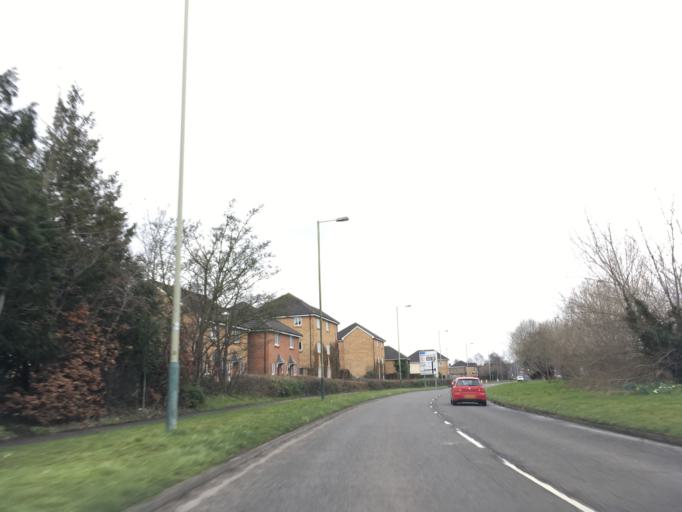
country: GB
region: England
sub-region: Borough of Swindon
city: Swindon
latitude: 51.5564
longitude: -1.7588
